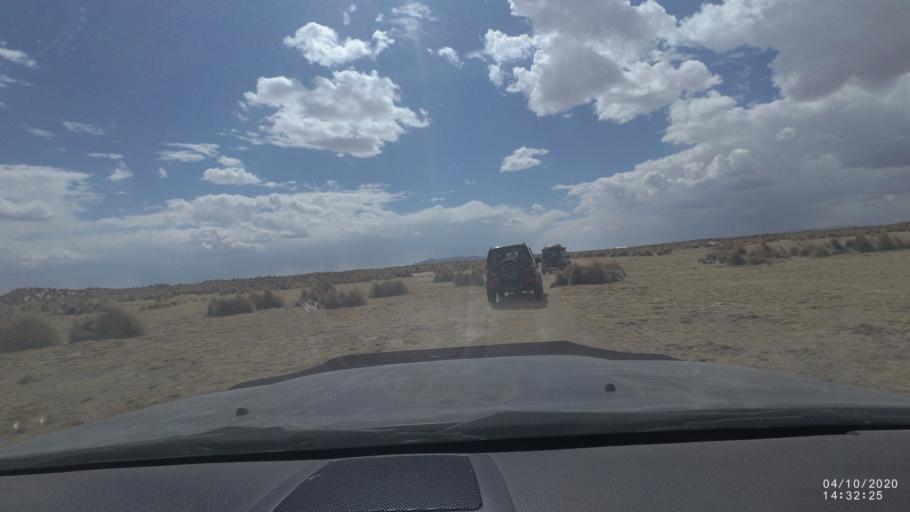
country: BO
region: Oruro
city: Poopo
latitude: -18.6732
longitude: -67.4649
